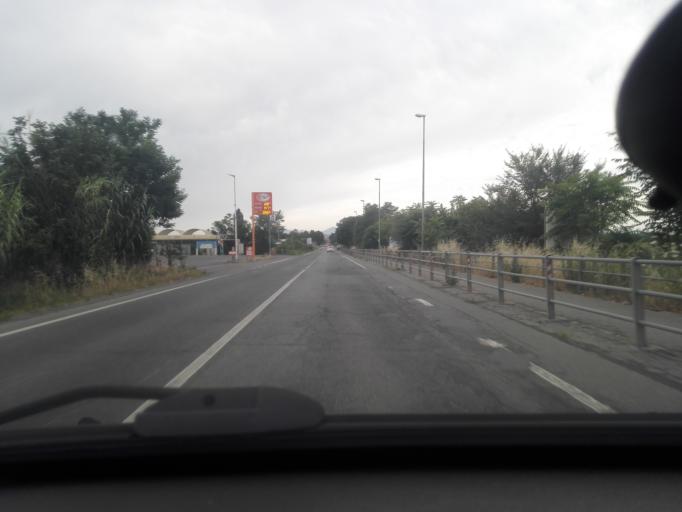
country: IT
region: Piedmont
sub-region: Provincia di Alessandria
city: Pozzolo Formigaro
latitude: 44.7846
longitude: 8.7888
